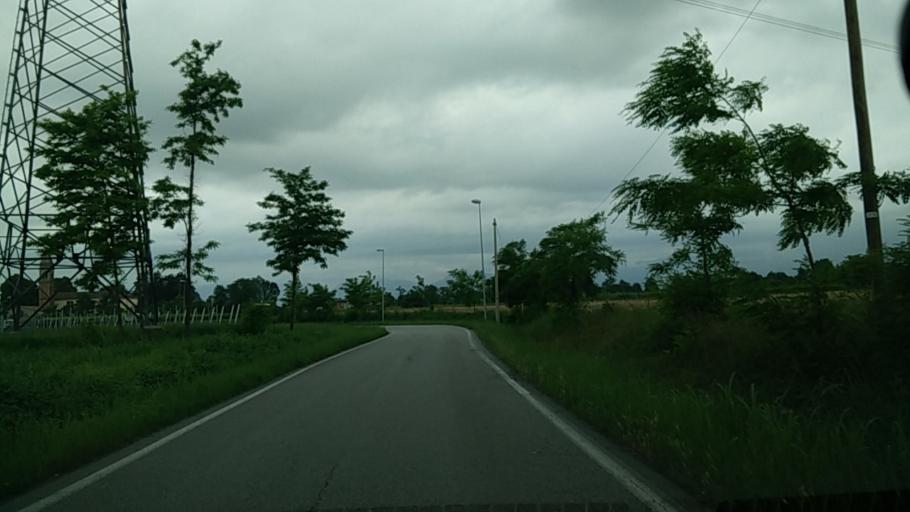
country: IT
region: Veneto
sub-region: Provincia di Treviso
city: Mareno di Piave
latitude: 45.8424
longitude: 12.3690
